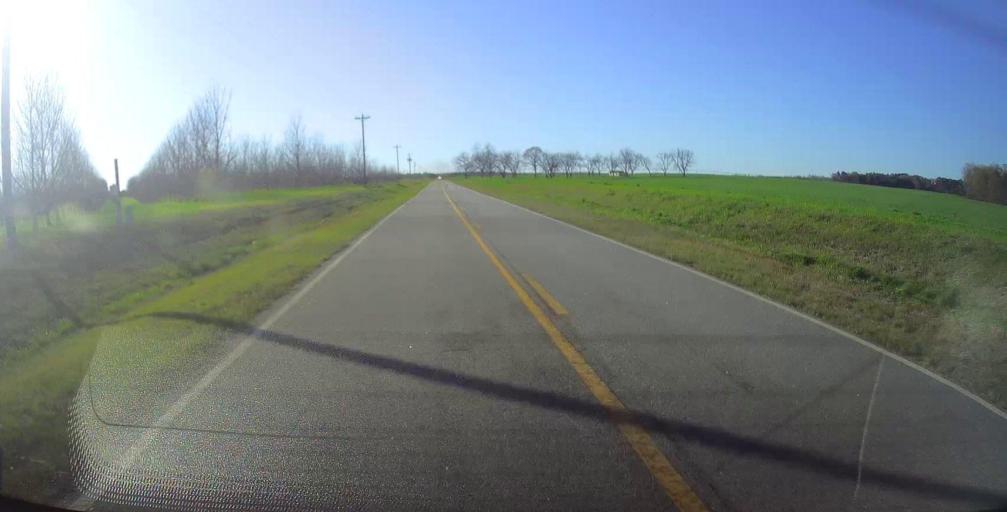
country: US
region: Georgia
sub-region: Dooly County
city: Unadilla
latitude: 32.3524
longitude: -83.6295
